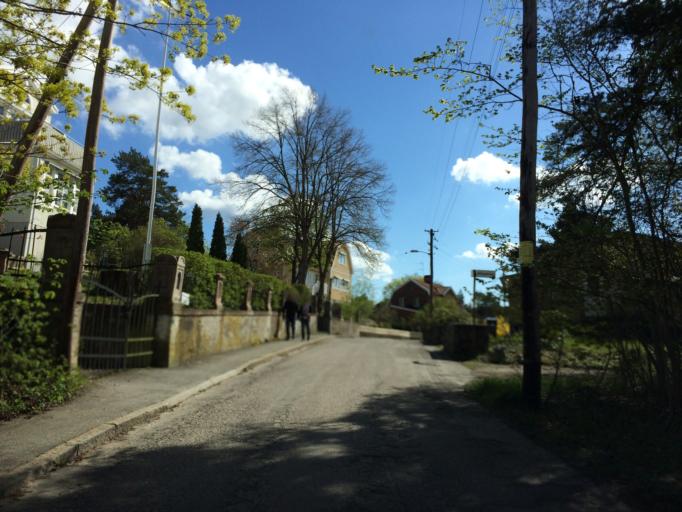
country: SE
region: Stockholm
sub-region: Huddinge Kommun
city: Segeltorp
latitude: 59.3030
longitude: 17.9626
